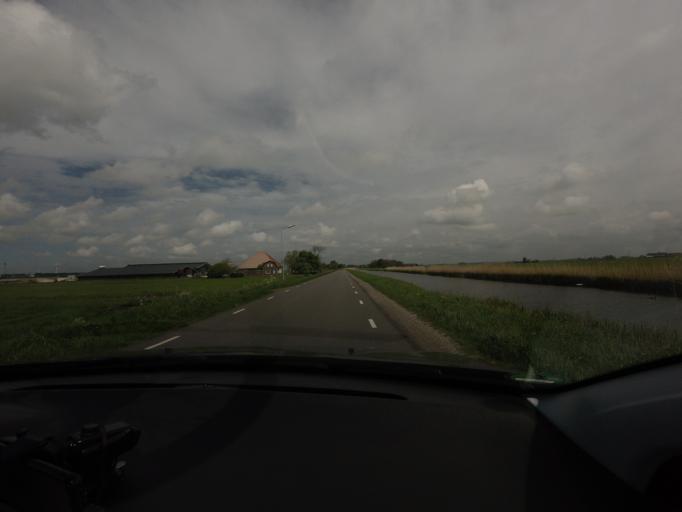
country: NL
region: North Holland
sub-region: Gemeente Alkmaar
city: Alkmaar
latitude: 52.5736
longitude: 4.7731
